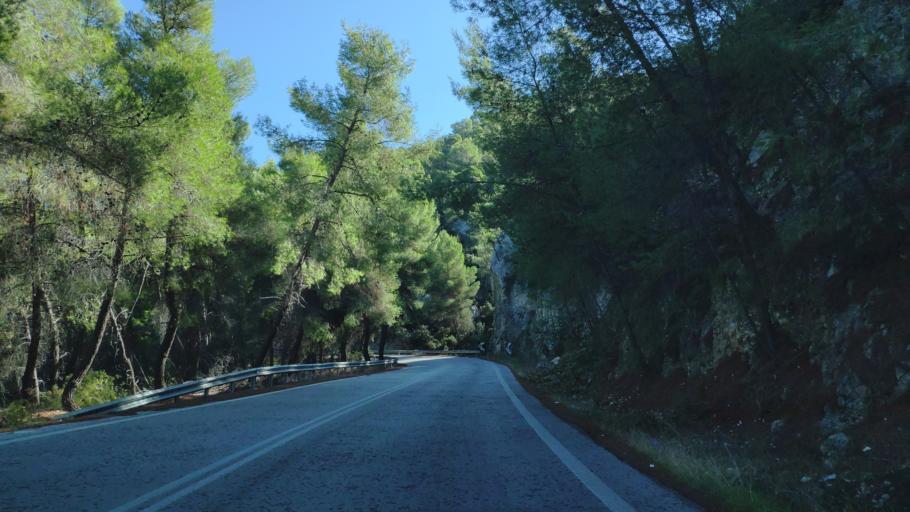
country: GR
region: Peloponnese
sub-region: Nomos Korinthias
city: Sofikon
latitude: 37.8274
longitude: 23.0679
